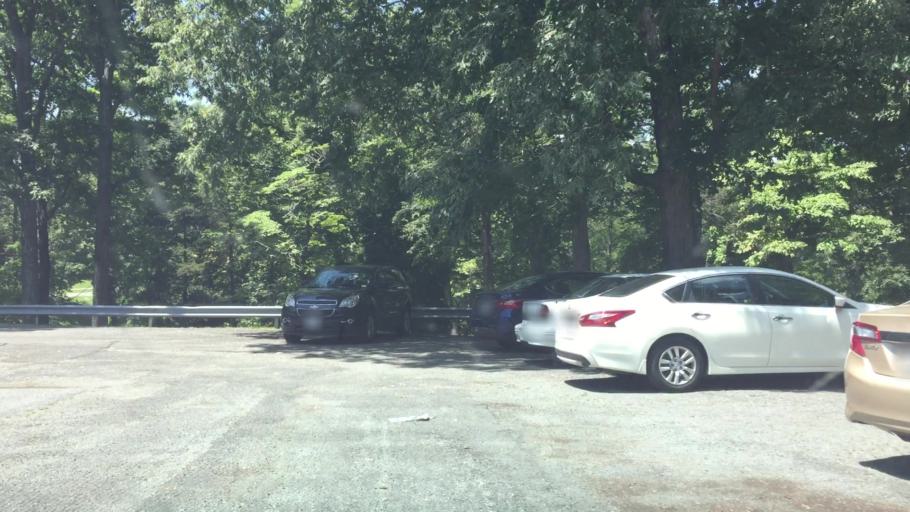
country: US
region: Virginia
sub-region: Pulaski County
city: Pulaski
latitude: 36.9504
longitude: -80.9026
